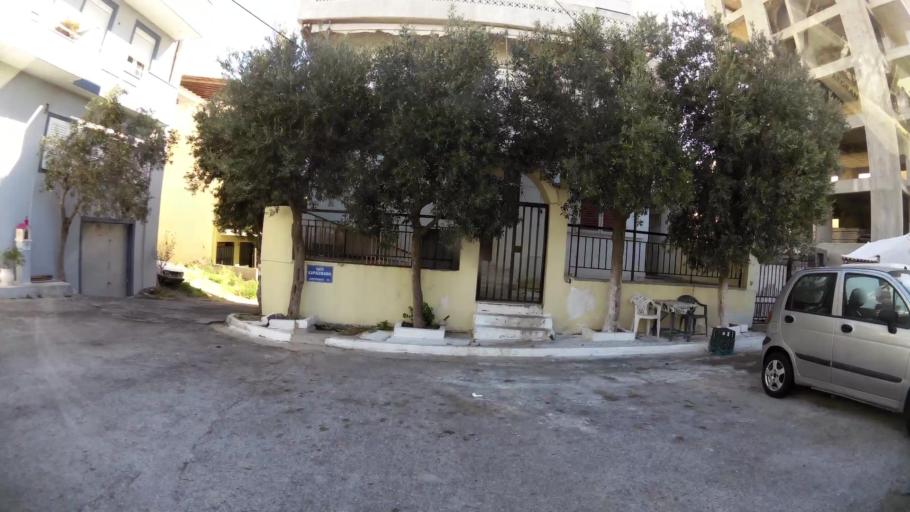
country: GR
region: Attica
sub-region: Nomos Piraios
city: Perama
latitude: 37.9696
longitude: 23.5628
